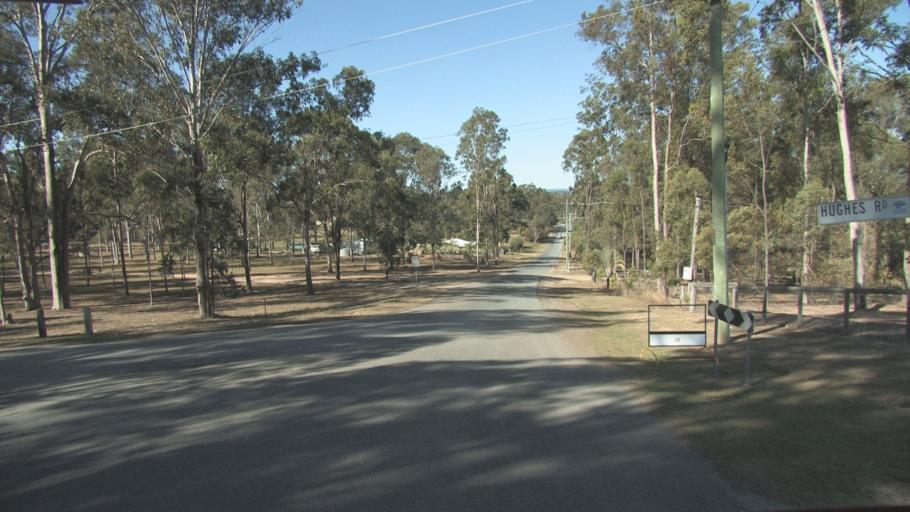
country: AU
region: Queensland
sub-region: Logan
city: Cedar Vale
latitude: -27.8551
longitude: 153.0148
